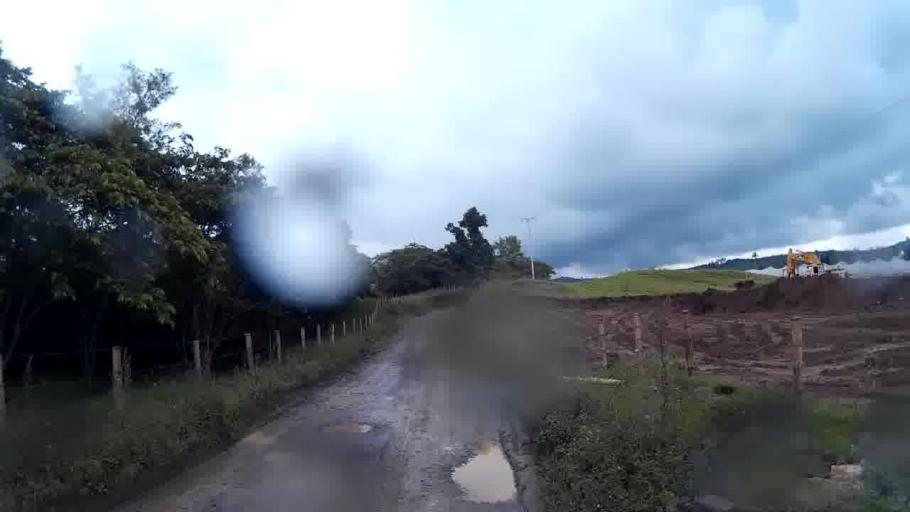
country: CO
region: Quindio
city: Filandia
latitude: 4.7046
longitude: -75.6735
